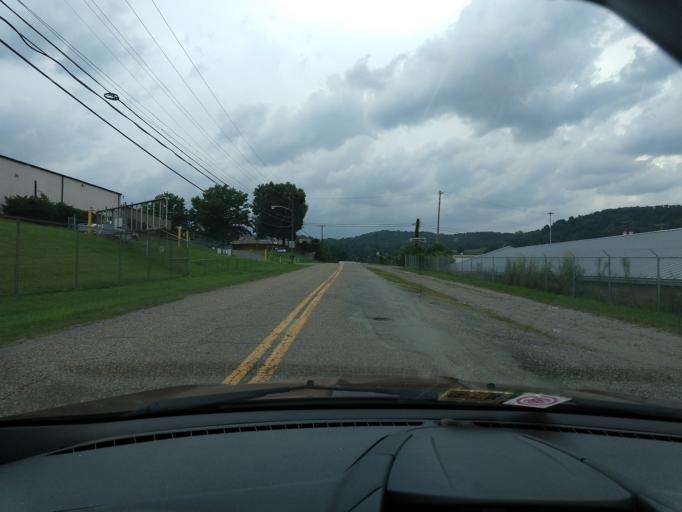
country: US
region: West Virginia
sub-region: Harrison County
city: Clarksburg
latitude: 39.2671
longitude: -80.3655
